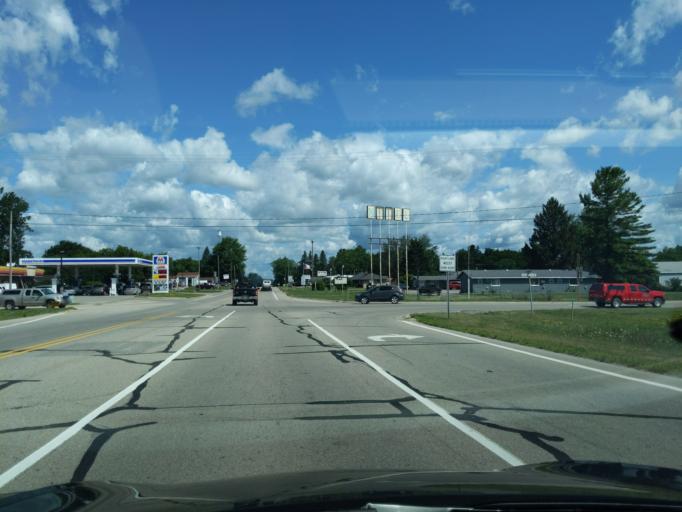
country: US
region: Michigan
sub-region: Clare County
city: Clare
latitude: 43.8106
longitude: -84.7683
